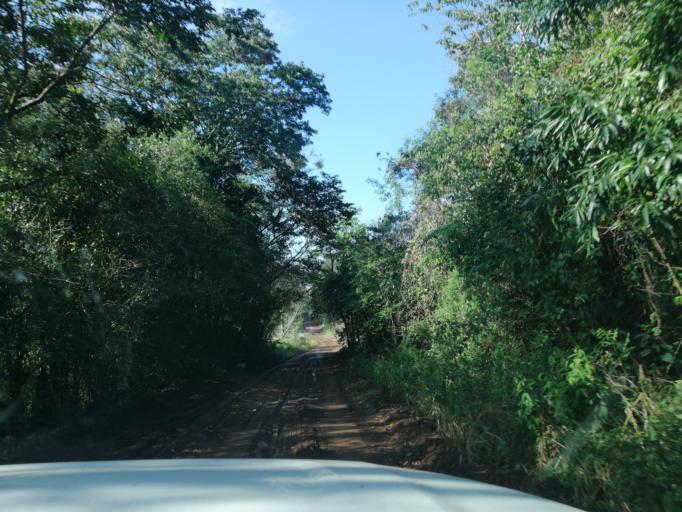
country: AR
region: Misiones
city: Cerro Azul
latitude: -27.6247
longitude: -55.5251
